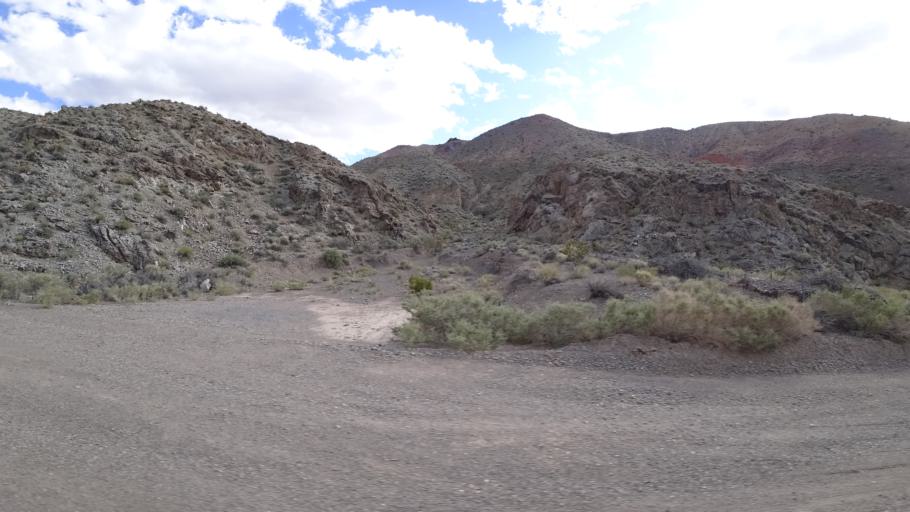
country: US
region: Nevada
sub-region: Nye County
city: Beatty
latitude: 36.4329
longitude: -117.1930
